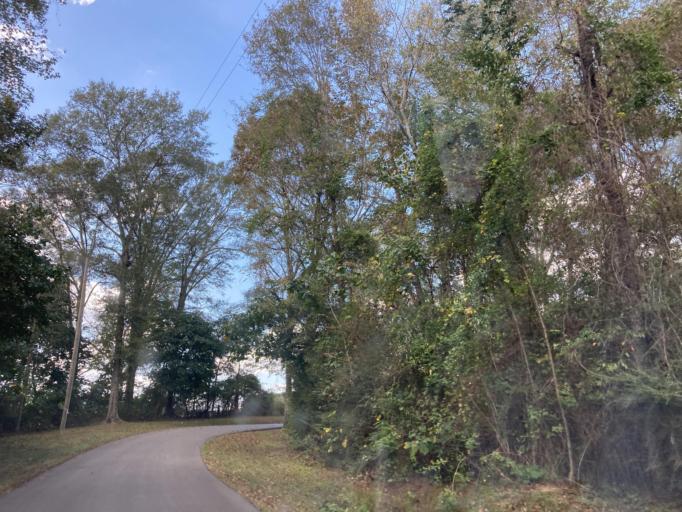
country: US
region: Mississippi
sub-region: Lamar County
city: Sumrall
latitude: 31.3739
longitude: -89.5434
